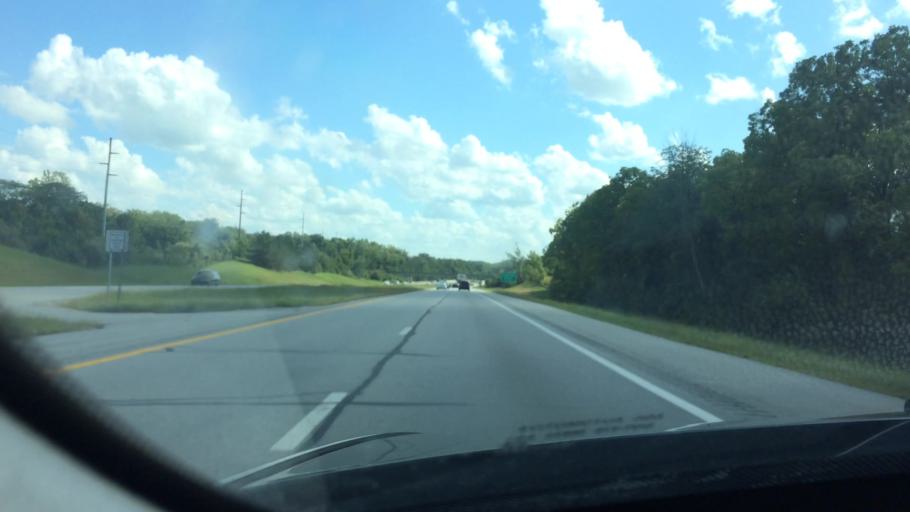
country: US
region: Ohio
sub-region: Shelby County
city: Sidney
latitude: 40.3361
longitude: -84.1594
